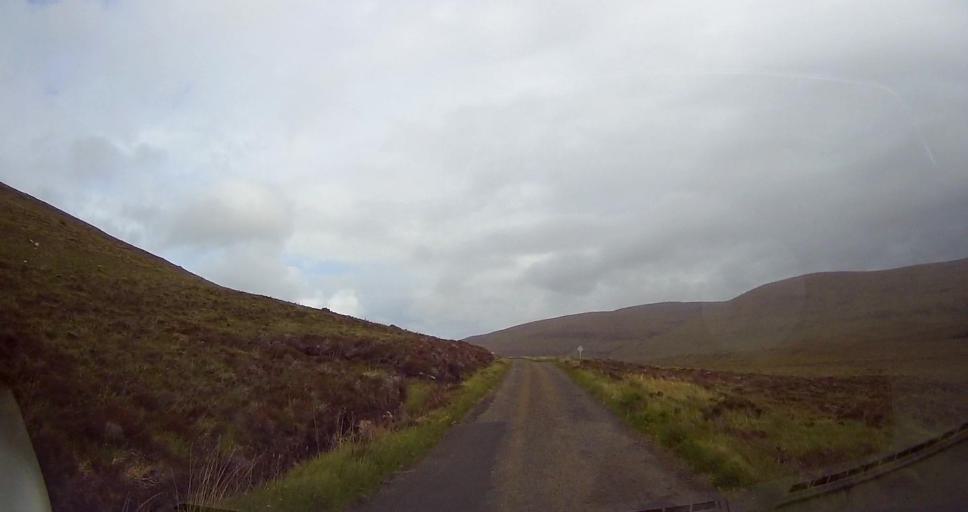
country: GB
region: Scotland
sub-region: Orkney Islands
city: Stromness
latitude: 58.8819
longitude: -3.3760
